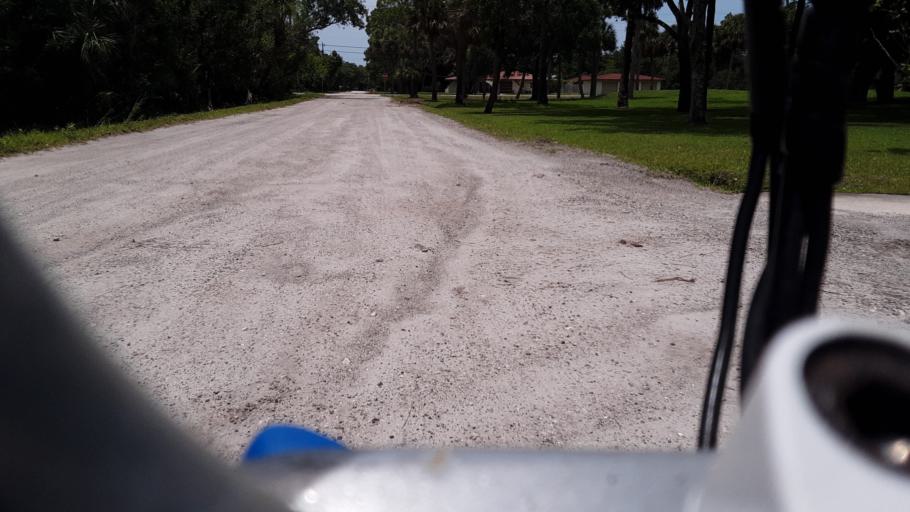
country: US
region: Florida
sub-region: Brevard County
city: Malabar
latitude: 27.9900
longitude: -80.6019
